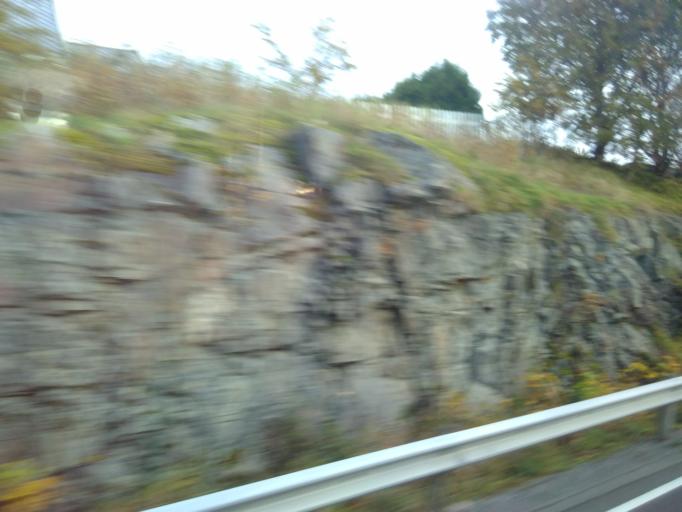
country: NO
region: Sor-Trondelag
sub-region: Hitra
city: Fillan
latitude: 63.5225
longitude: 9.0993
